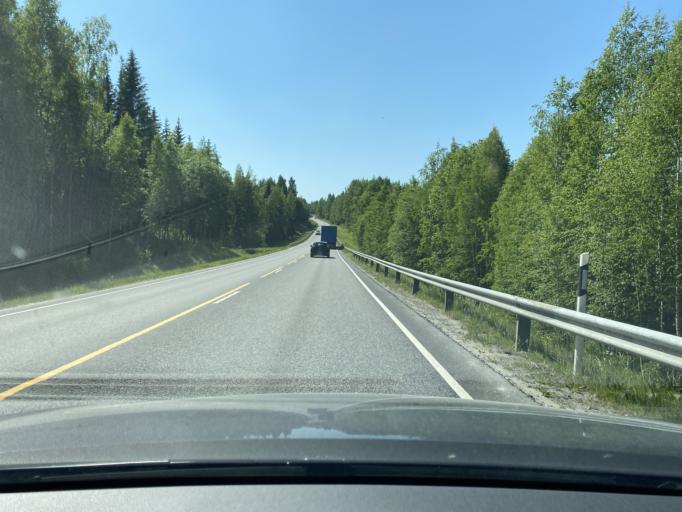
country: FI
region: Pirkanmaa
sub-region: Lounais-Pirkanmaa
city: Mouhijaervi
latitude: 61.3846
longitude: 23.1842
